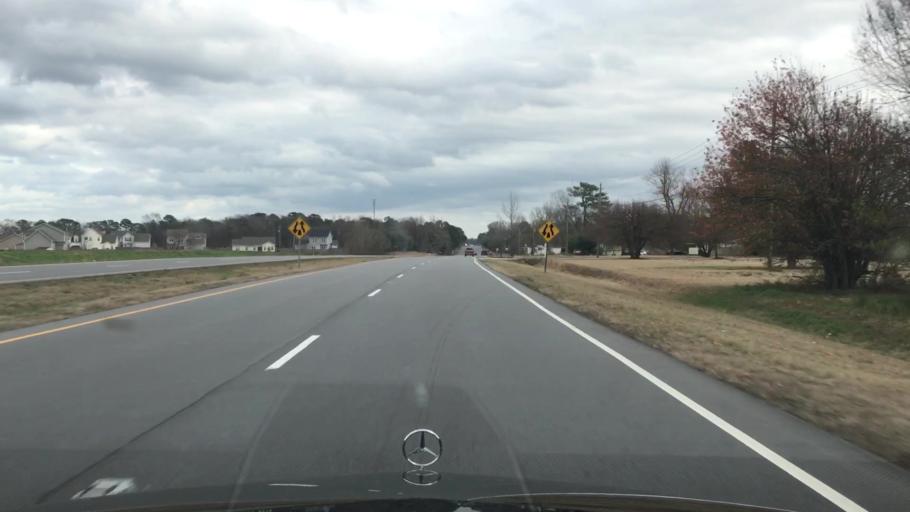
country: US
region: North Carolina
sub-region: Onslow County
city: Richlands
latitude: 34.9167
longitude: -77.6054
